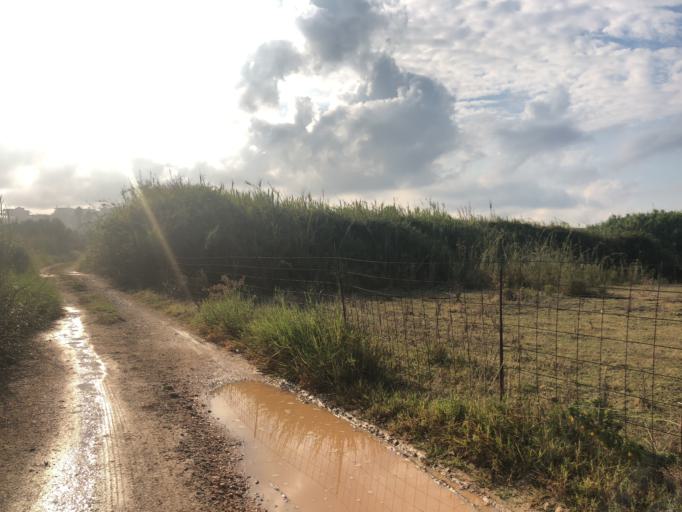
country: GR
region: Crete
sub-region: Nomos Chanias
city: Georgioupolis
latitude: 35.3470
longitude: 24.3046
